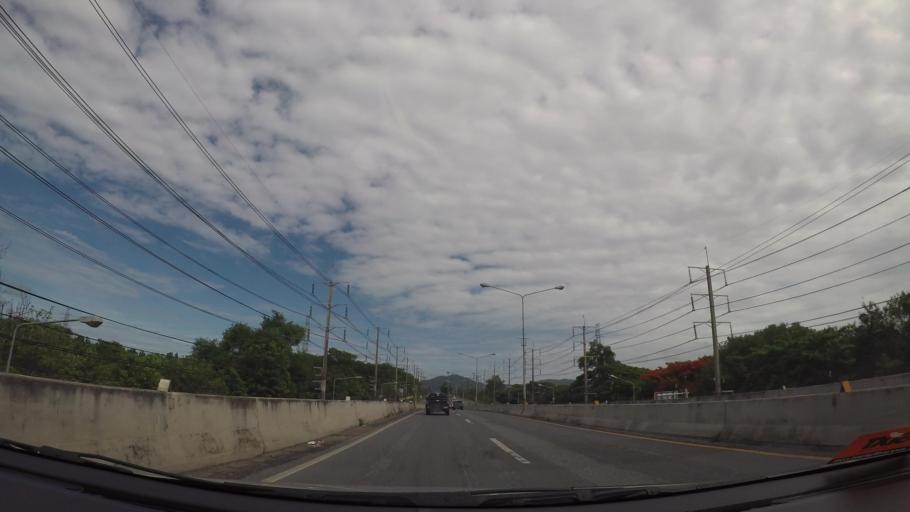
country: TH
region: Rayong
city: Ban Chang
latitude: 12.7289
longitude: 101.1416
